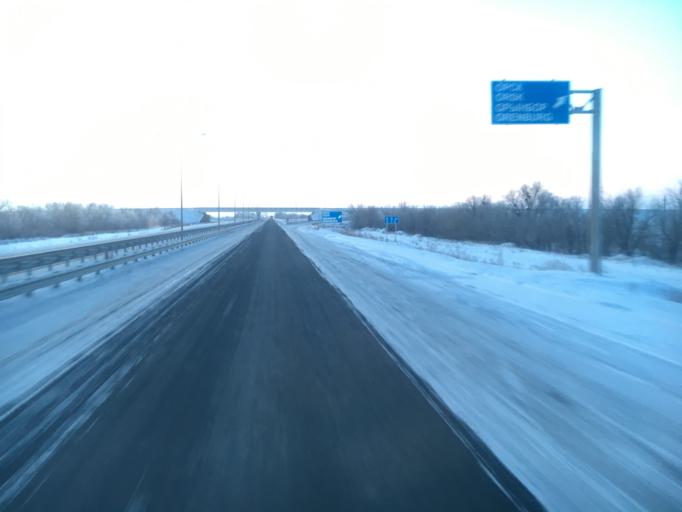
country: KZ
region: Aqtoebe
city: Aqtobe
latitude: 50.2942
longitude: 57.4421
